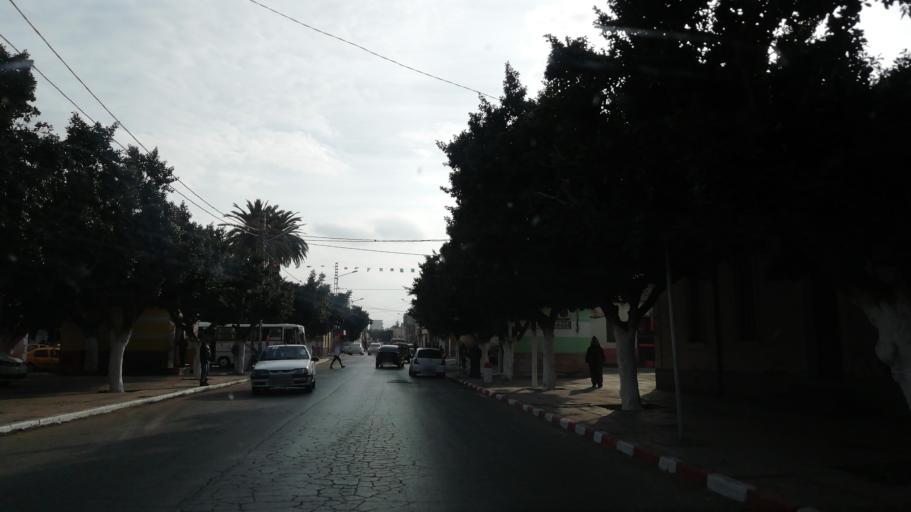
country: DZ
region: Mostaganem
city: Mostaganem
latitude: 35.8596
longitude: 0.0729
